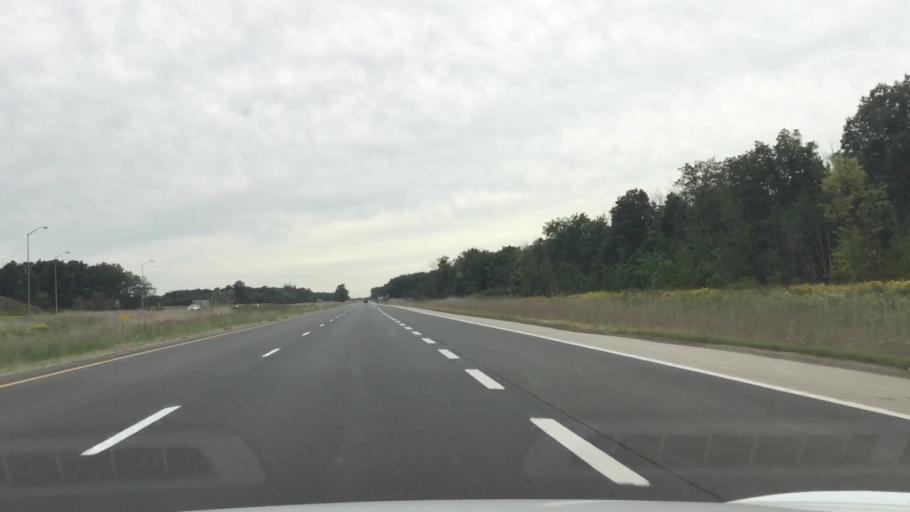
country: CA
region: Ontario
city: Lambton Shores
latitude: 42.9921
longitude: -81.8813
